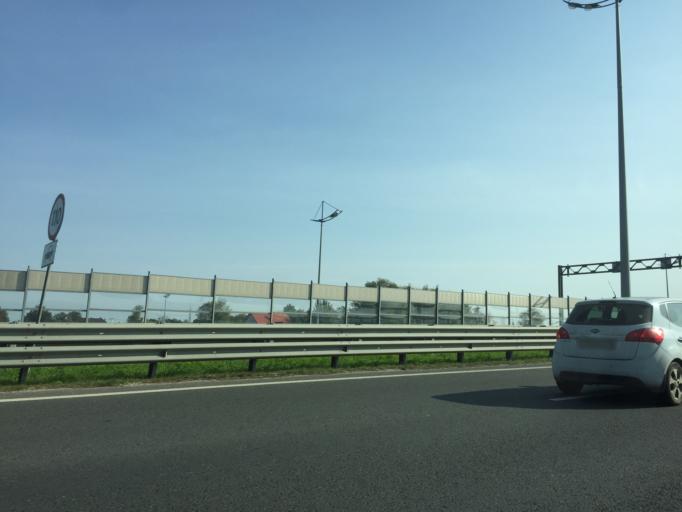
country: RU
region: Kaliningrad
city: Bol'shoe Isakovo
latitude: 54.6964
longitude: 20.5983
